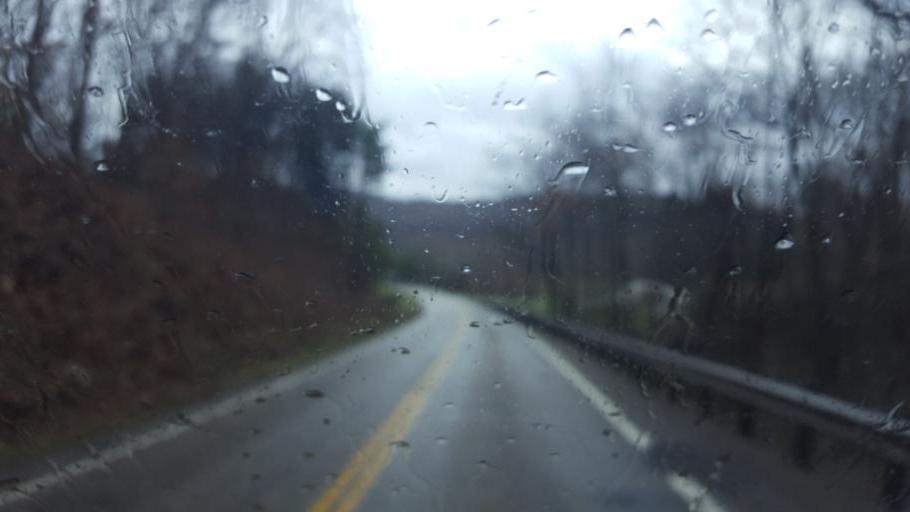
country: US
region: Ohio
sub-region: Ashland County
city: Loudonville
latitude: 40.6214
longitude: -82.1930
